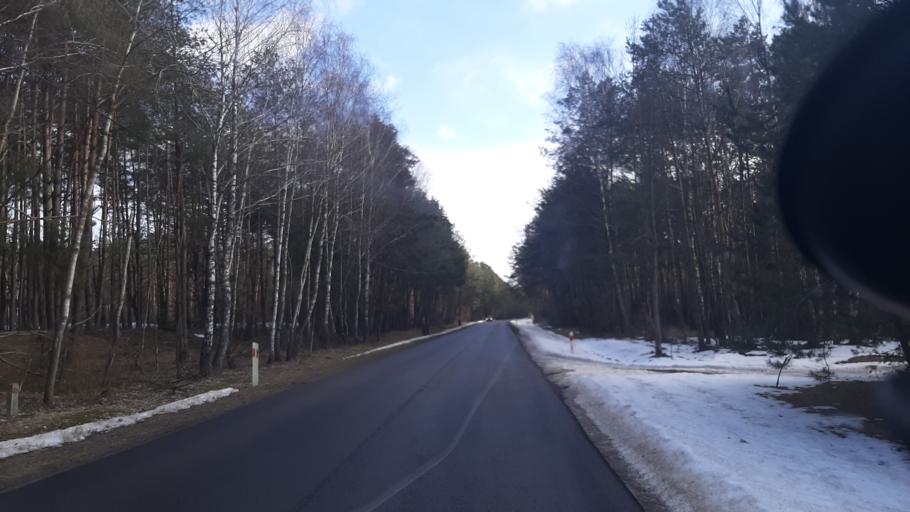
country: PL
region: Lublin Voivodeship
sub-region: Powiat wlodawski
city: Urszulin
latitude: 51.4955
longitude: 23.2660
